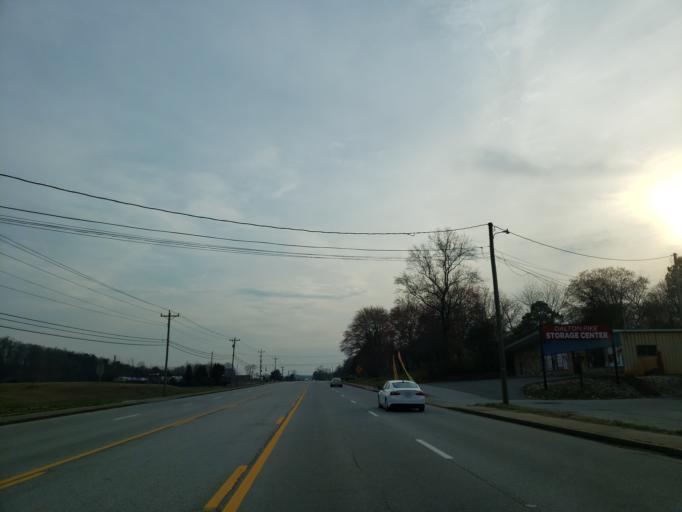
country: US
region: Tennessee
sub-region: Bradley County
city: Wildwood Lake
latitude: 35.1020
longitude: -84.8724
